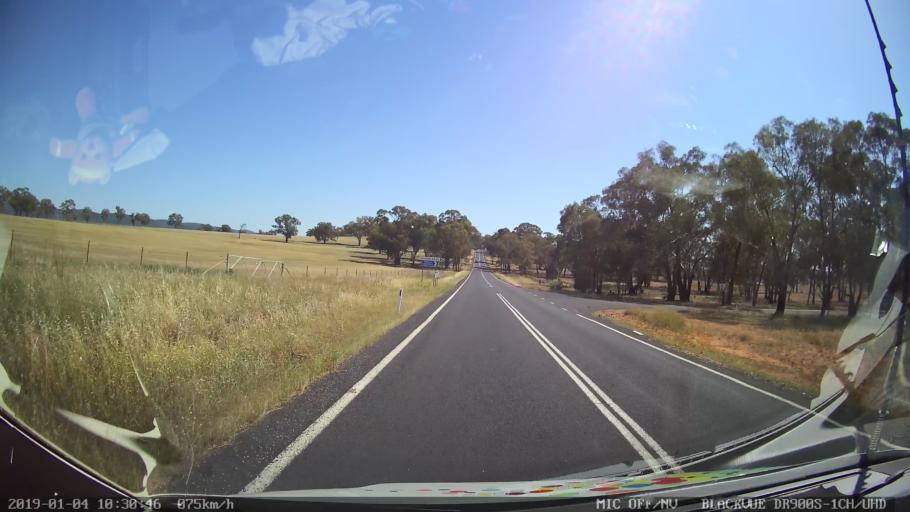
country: AU
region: New South Wales
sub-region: Cabonne
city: Canowindra
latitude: -33.3422
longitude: 148.6295
